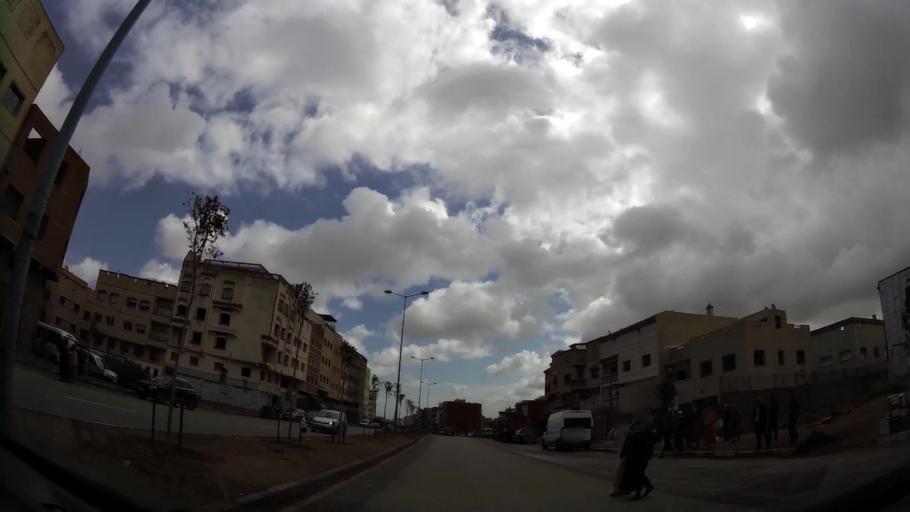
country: MA
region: Grand Casablanca
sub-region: Casablanca
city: Casablanca
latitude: 33.5330
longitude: -7.5833
